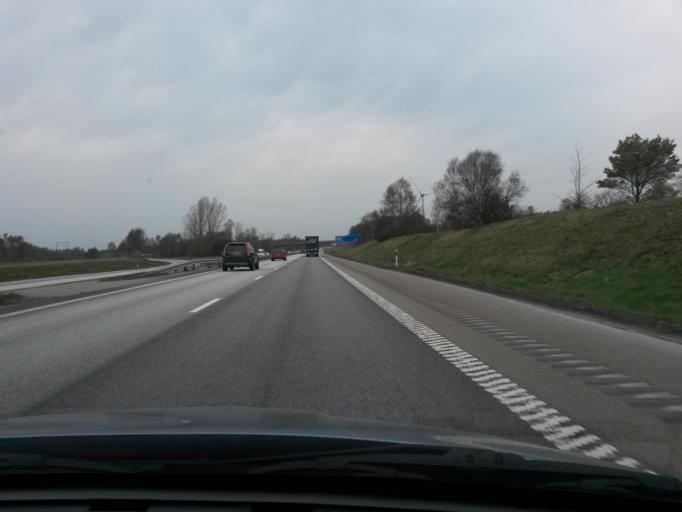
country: SE
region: Halland
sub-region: Varbergs Kommun
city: Tvaaker
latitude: 57.0455
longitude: 12.3687
